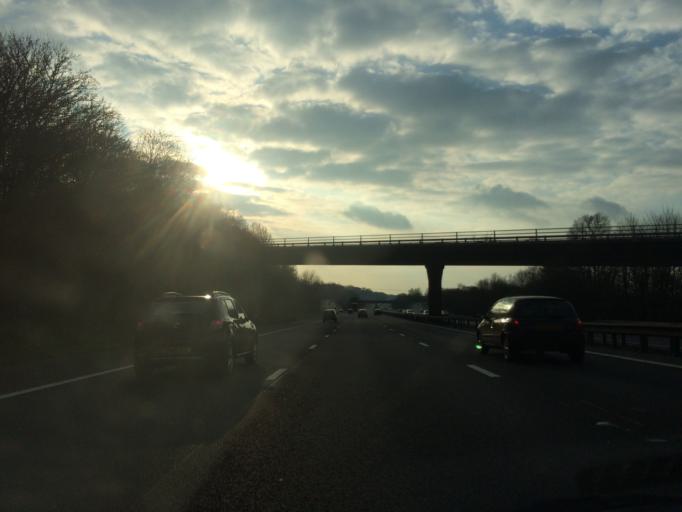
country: GB
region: England
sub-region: Borough of Swindon
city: Chiseldon
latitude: 51.5259
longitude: -1.7156
